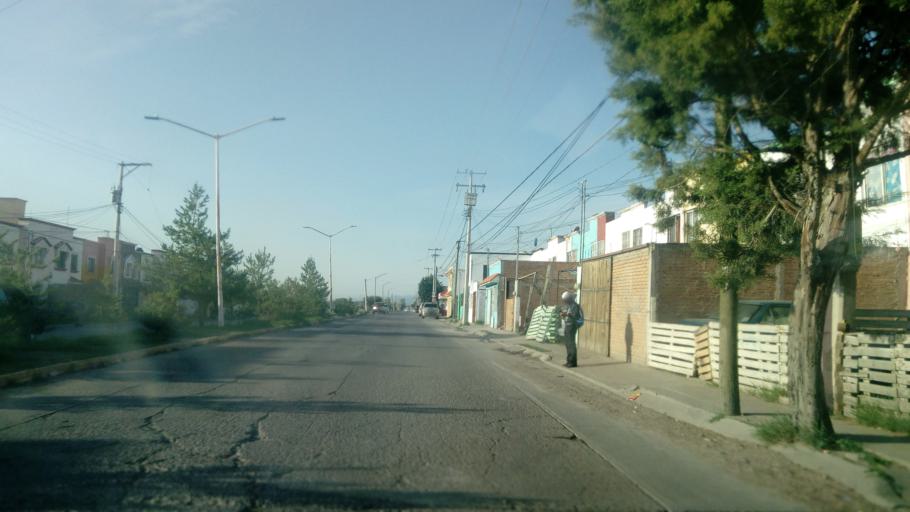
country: MX
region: Durango
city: Victoria de Durango
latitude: 24.0692
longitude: -104.5867
